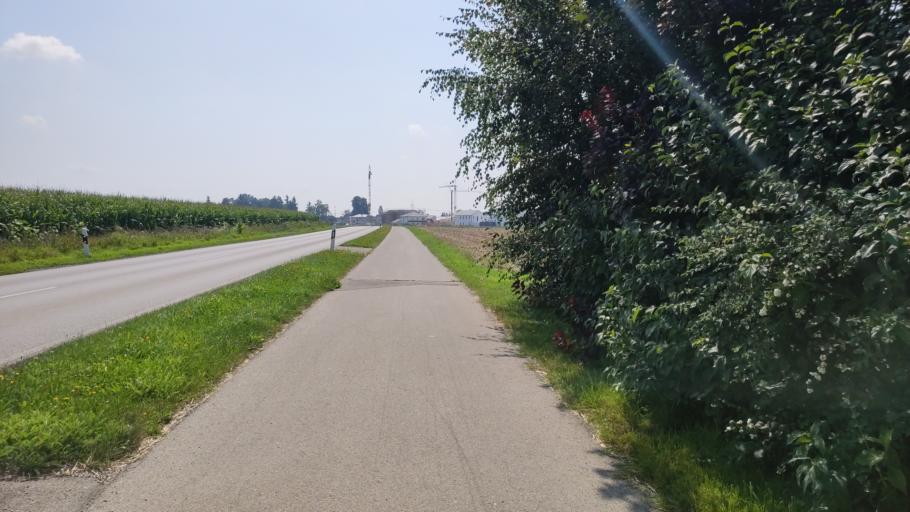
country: DE
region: Bavaria
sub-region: Swabia
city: Oberottmarshausen
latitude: 48.2436
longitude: 10.8517
